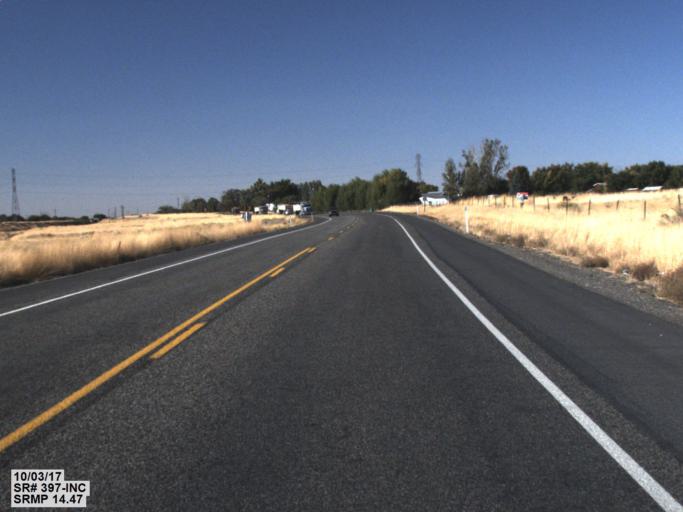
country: US
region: Washington
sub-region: Benton County
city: Finley
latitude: 46.1787
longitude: -119.0639
